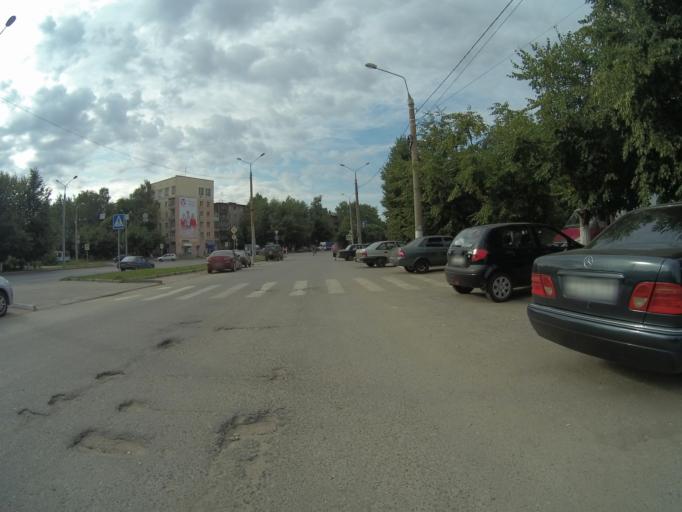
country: RU
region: Vladimir
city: Bogolyubovo
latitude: 56.1703
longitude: 40.4755
